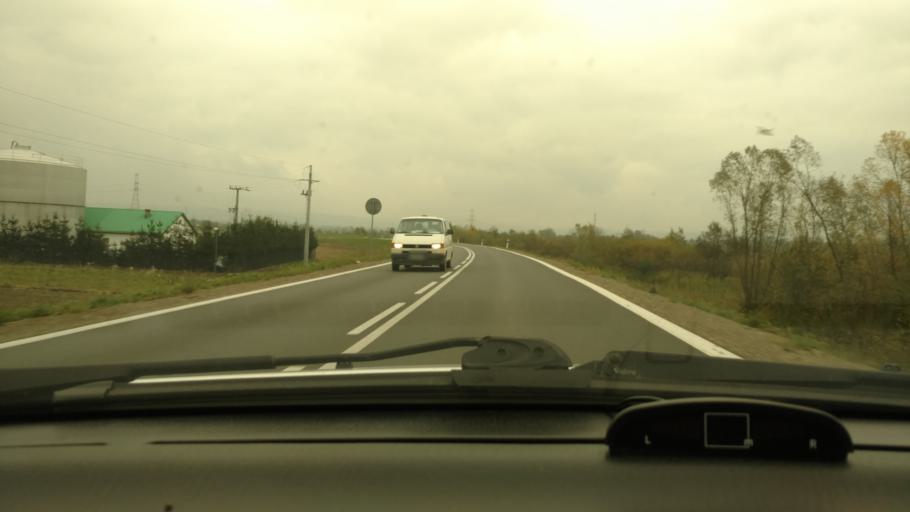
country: PL
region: Lesser Poland Voivodeship
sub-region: Powiat nowosadecki
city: Stary Sacz
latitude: 49.5917
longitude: 20.6428
